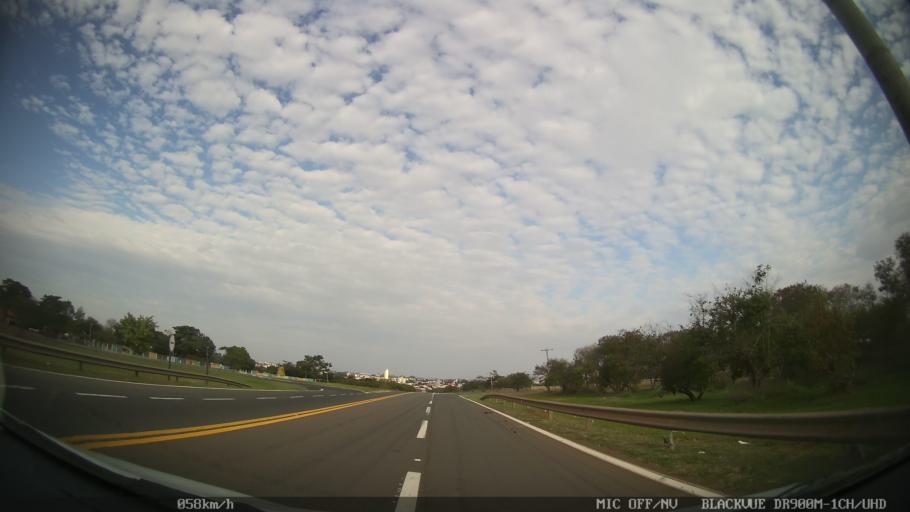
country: BR
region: Sao Paulo
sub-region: Cosmopolis
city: Cosmopolis
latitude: -22.6349
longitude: -47.2057
